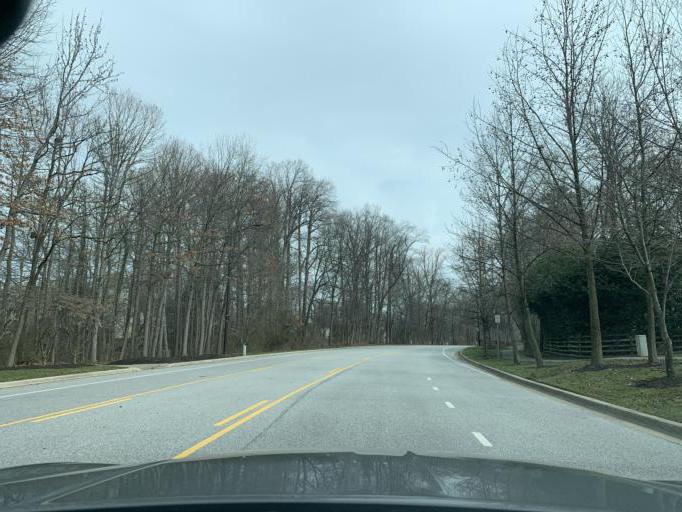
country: US
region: Maryland
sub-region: Anne Arundel County
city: Maryland City
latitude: 39.1085
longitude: -76.8033
